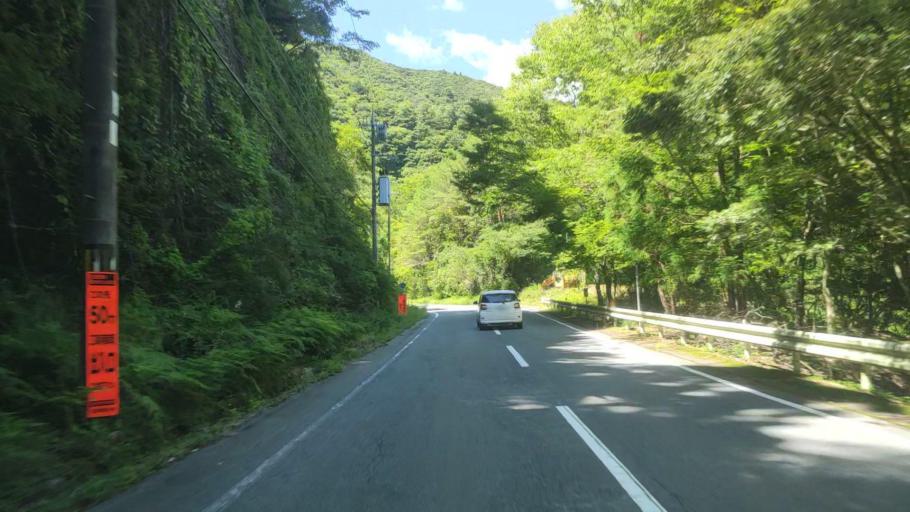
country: JP
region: Mie
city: Owase
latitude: 34.1842
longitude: 136.0029
